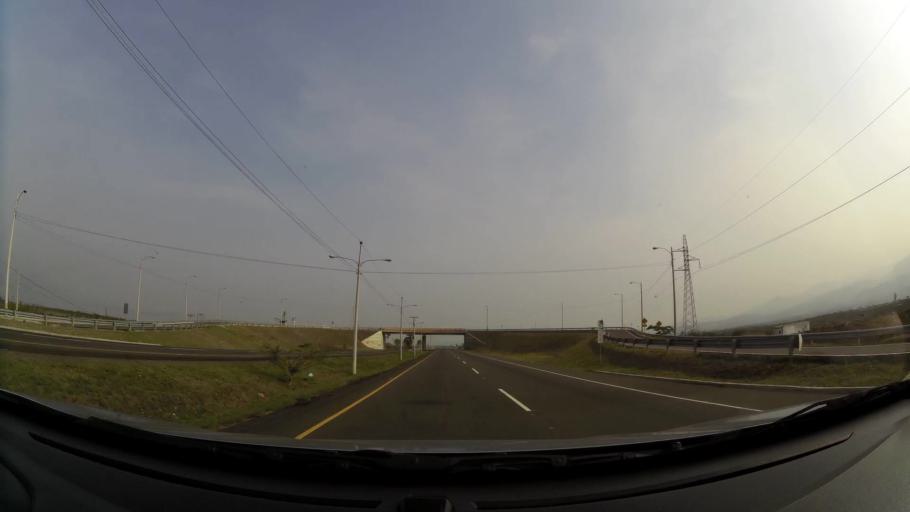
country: HN
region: Comayagua
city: Comayagua
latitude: 14.4007
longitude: -87.6181
